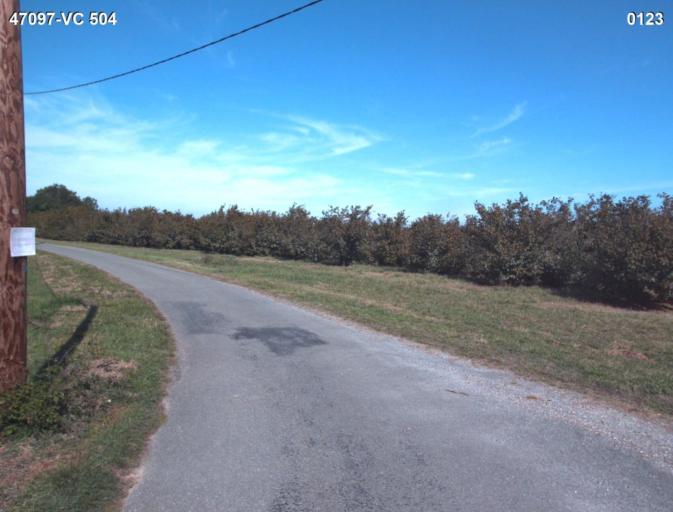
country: FR
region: Aquitaine
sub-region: Departement du Lot-et-Garonne
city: Vianne
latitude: 44.1922
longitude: 0.3521
